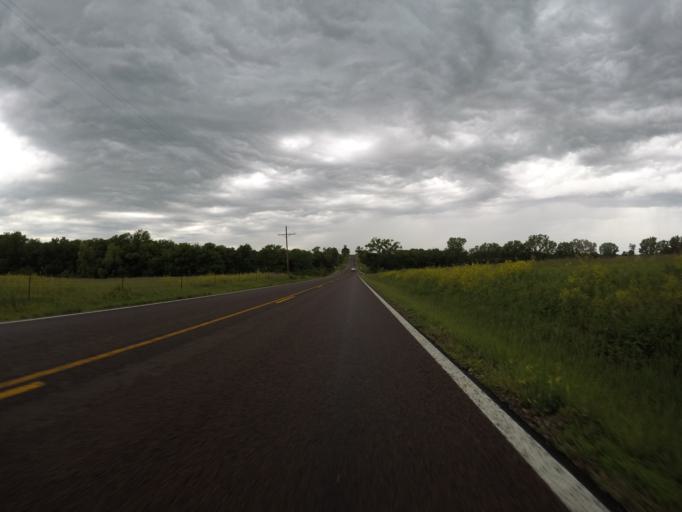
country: US
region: Kansas
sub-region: Shawnee County
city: Rossville
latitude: 38.9574
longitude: -96.0309
